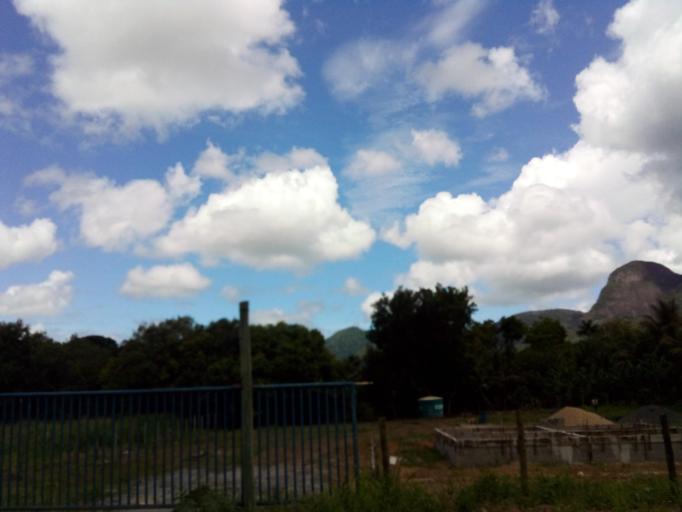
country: BR
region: Espirito Santo
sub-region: Ibiracu
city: Ibiracu
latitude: -19.8774
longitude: -40.3617
